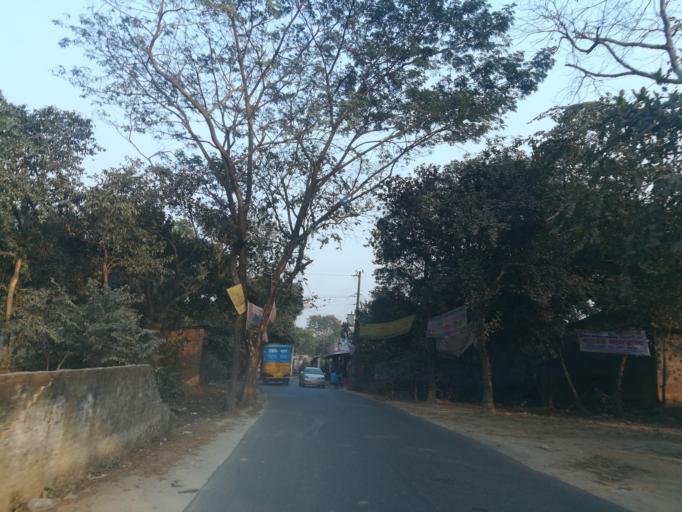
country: BD
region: Dhaka
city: Tungi
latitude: 23.8578
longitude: 90.3141
